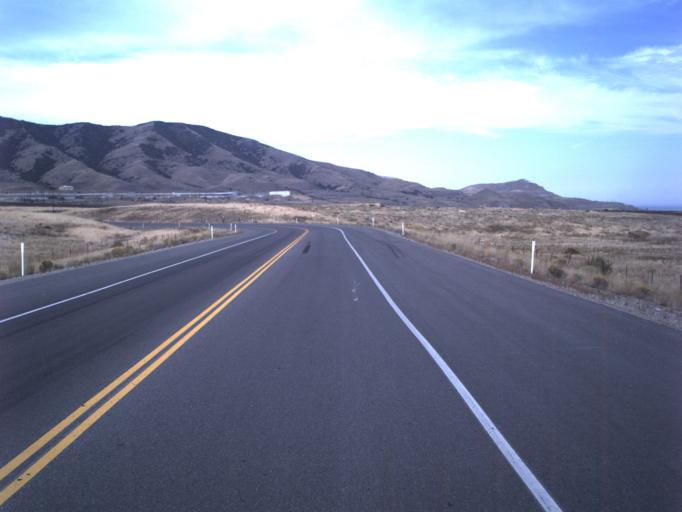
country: US
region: Utah
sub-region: Salt Lake County
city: Oquirrh
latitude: 40.6539
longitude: -112.0705
